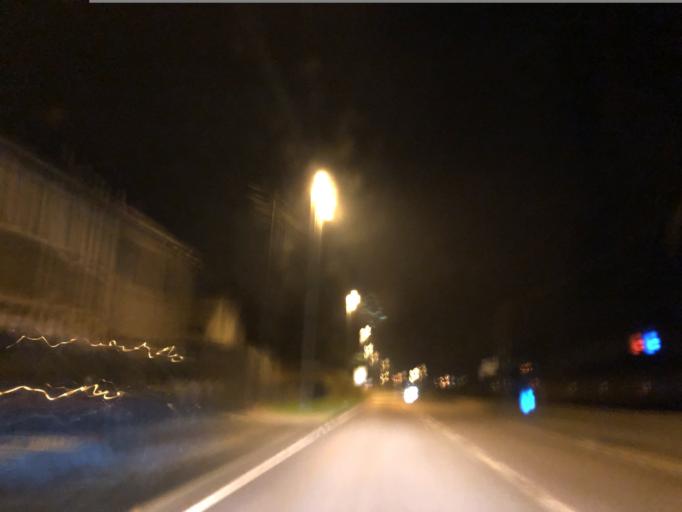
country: GB
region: England
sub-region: Borough of Oldham
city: Shaw
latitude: 53.5782
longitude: -2.0540
